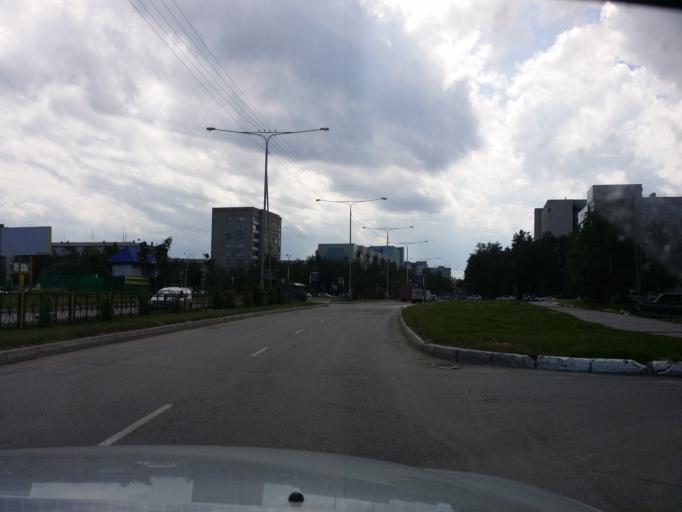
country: RU
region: Khanty-Mansiyskiy Avtonomnyy Okrug
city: Nizhnevartovsk
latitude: 60.9469
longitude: 76.5661
